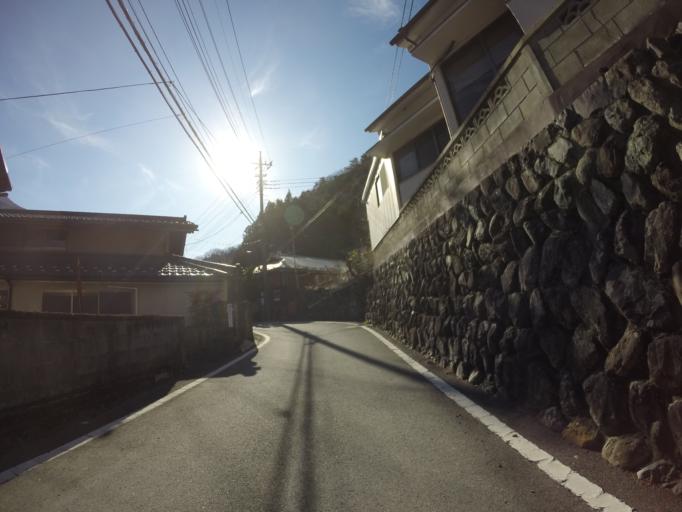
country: JP
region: Yamanashi
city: Ryuo
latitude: 35.3956
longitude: 138.3227
